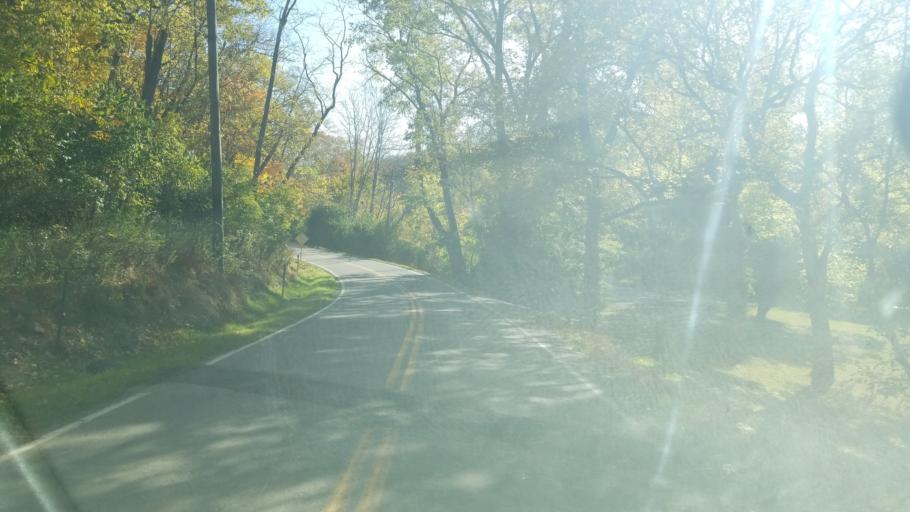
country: US
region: Ohio
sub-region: Warren County
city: Morrow
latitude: 39.3611
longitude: -84.1207
